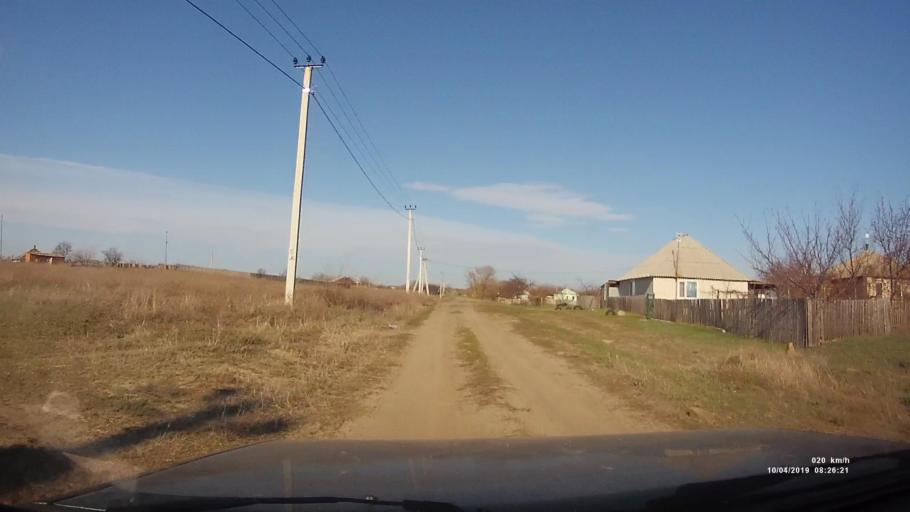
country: RU
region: Rostov
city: Kamensk-Shakhtinskiy
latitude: 48.3581
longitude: 40.2289
